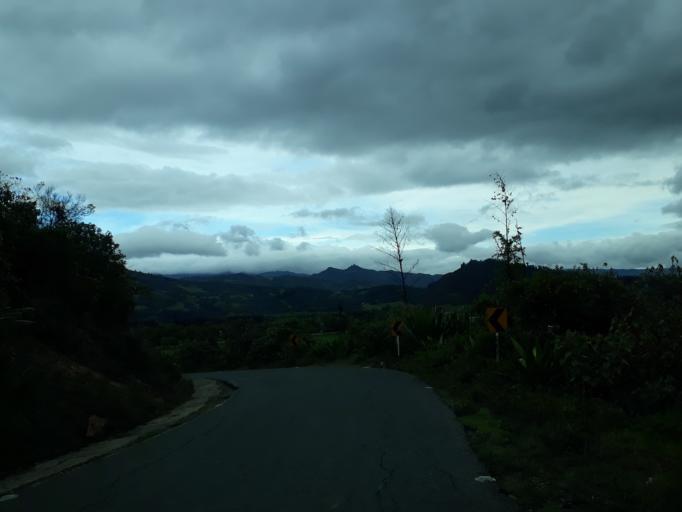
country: CO
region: Cundinamarca
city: Susa
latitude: 5.4028
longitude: -73.7671
